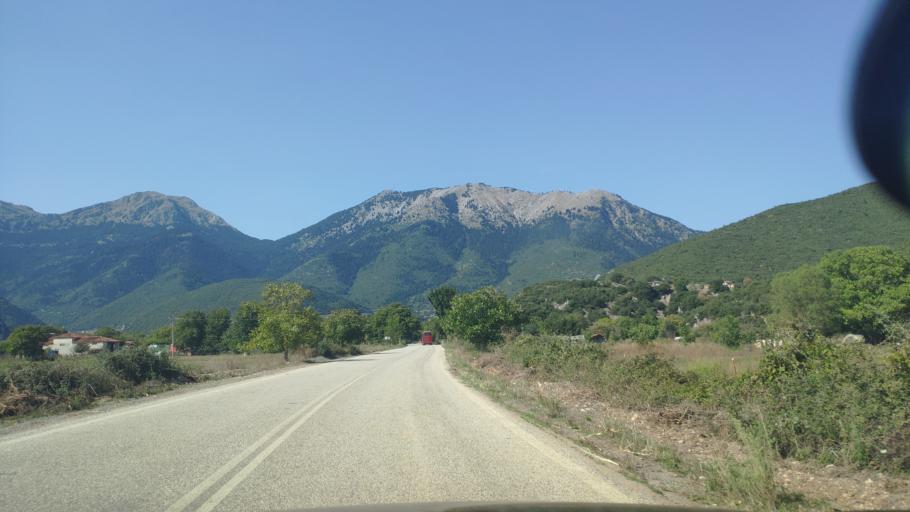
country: GR
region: Peloponnese
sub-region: Nomos Korinthias
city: Nemea
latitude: 37.8454
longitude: 22.4144
